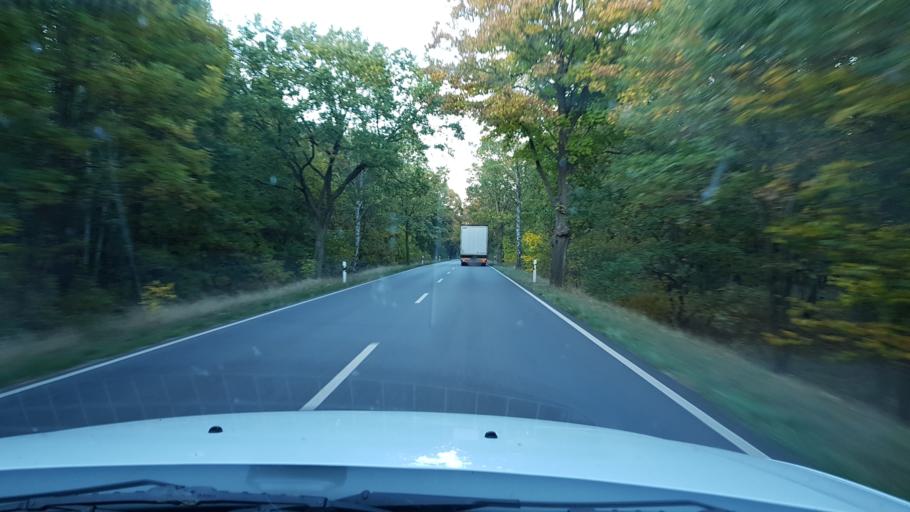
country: PL
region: West Pomeranian Voivodeship
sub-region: Powiat gryfinski
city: Widuchowa
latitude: 53.1680
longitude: 14.3375
